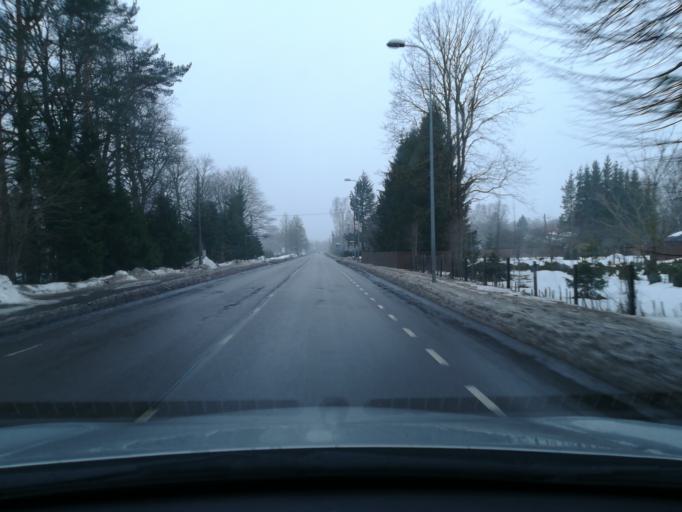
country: EE
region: Harju
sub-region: Rae vald
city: Jueri
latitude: 59.3614
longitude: 24.9357
